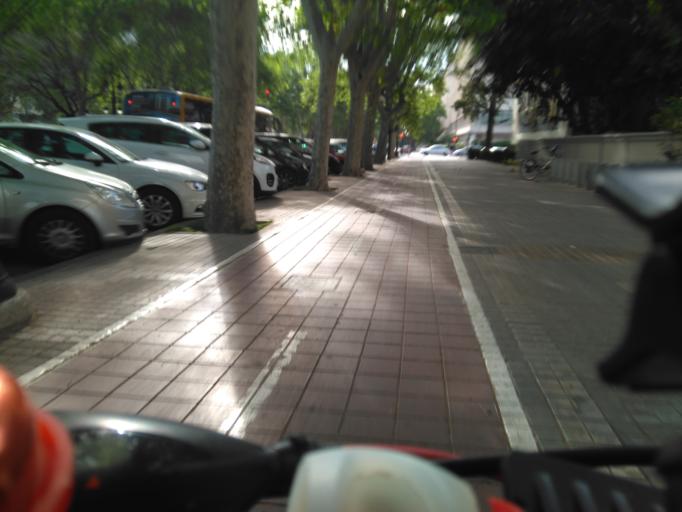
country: ES
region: Valencia
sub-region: Provincia de Valencia
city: Valencia
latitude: 39.4770
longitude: -0.3594
